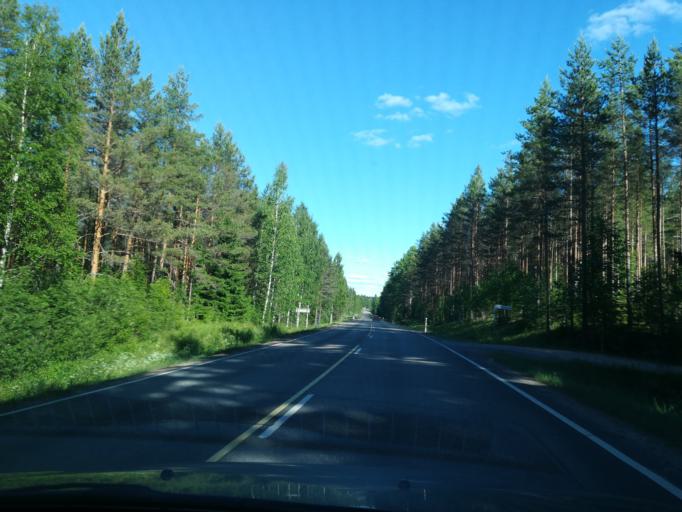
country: FI
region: South Karelia
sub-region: Imatra
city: Ruokolahti
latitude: 61.3663
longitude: 28.6834
